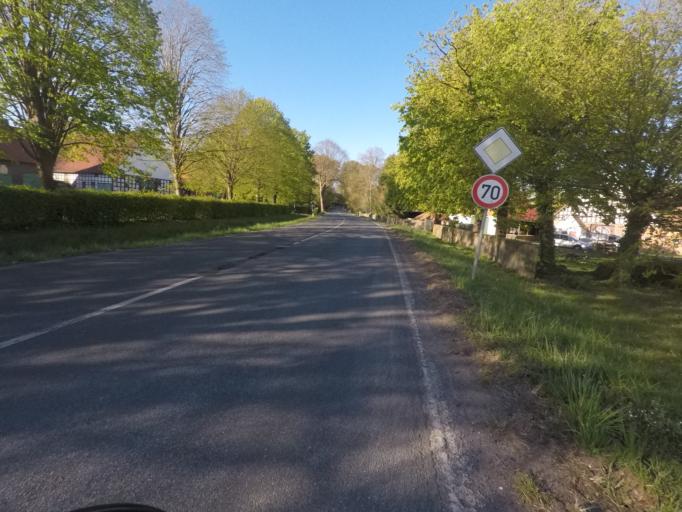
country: DE
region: North Rhine-Westphalia
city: Enger
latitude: 52.1082
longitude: 8.5964
